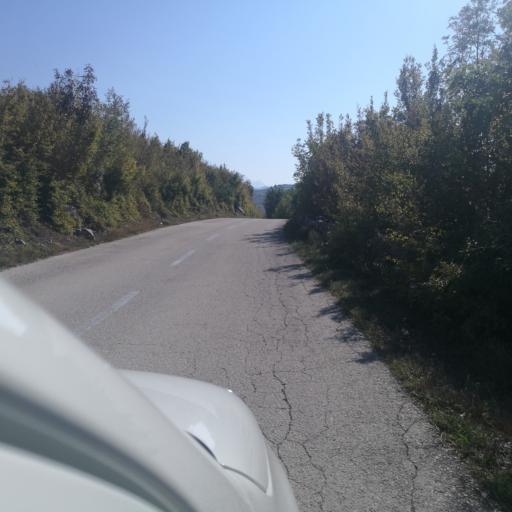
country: HR
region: Splitsko-Dalmatinska
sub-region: Grad Omis
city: Omis
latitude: 43.5224
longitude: 16.7510
